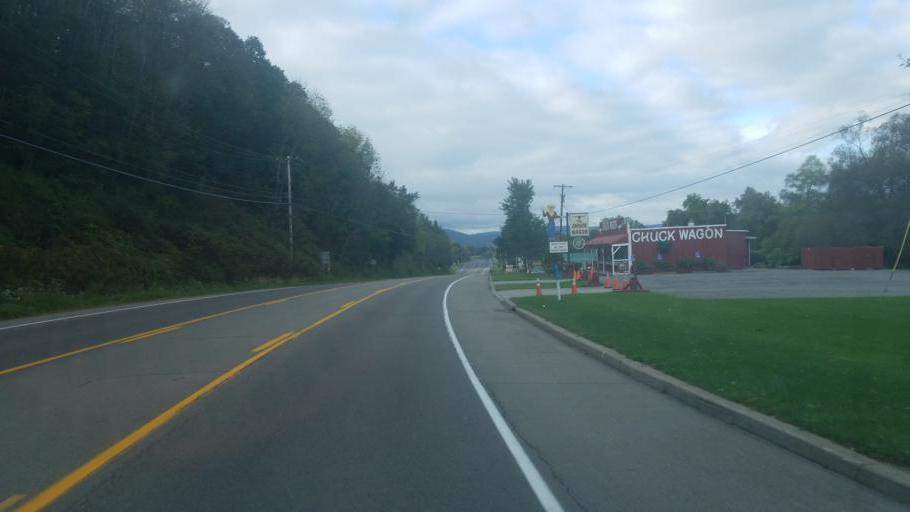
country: US
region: New York
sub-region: Cattaraugus County
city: Olean
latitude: 42.1046
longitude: -78.4184
